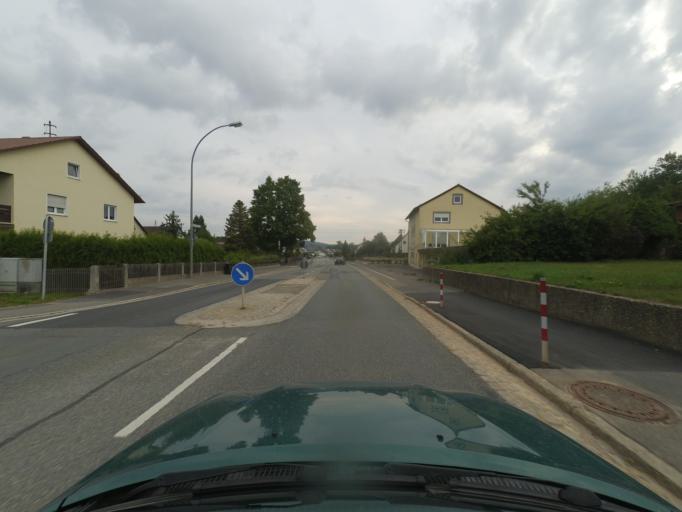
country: DE
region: Bavaria
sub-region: Upper Palatinate
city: Schnaittenbach
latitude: 49.5441
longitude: 11.9887
